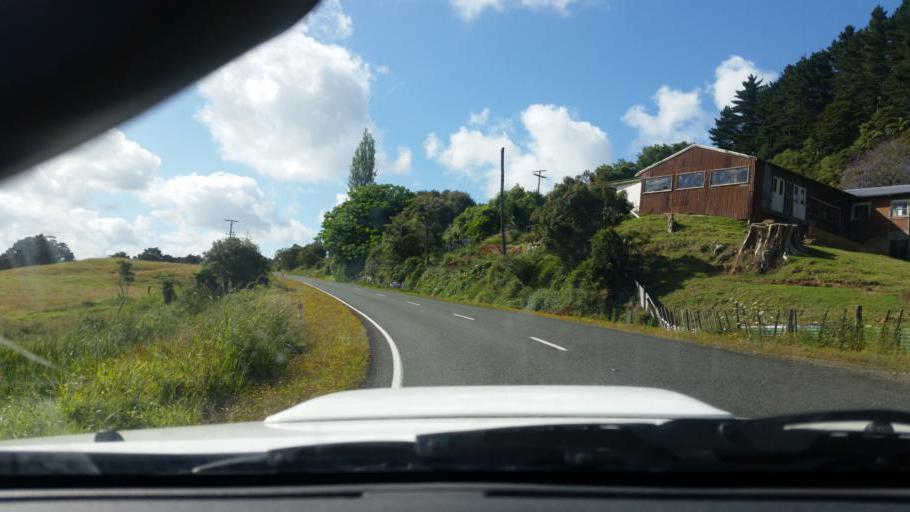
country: NZ
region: Northland
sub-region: Kaipara District
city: Dargaville
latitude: -35.7651
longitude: 173.6870
